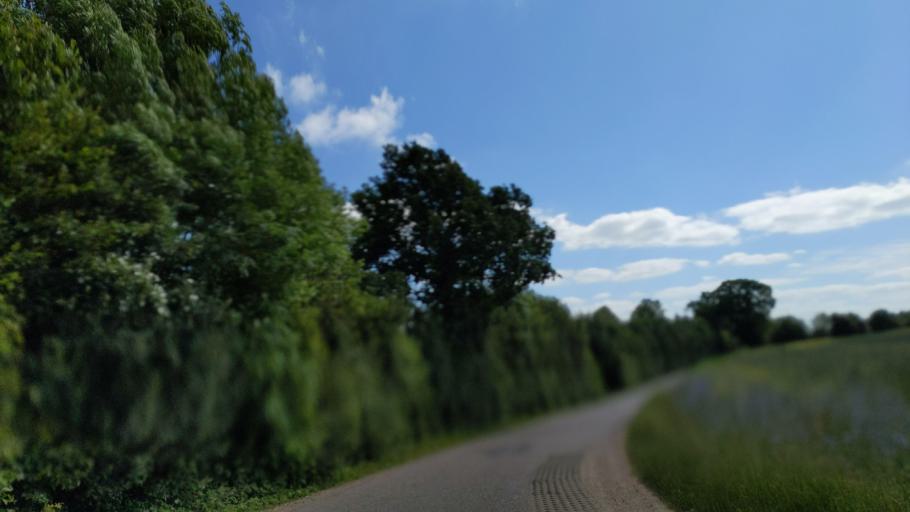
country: DE
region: Schleswig-Holstein
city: Timmendorfer Strand
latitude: 53.9912
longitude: 10.7538
